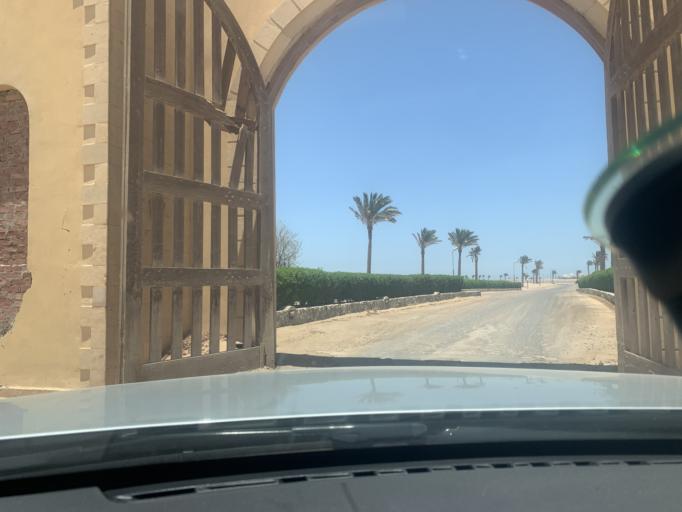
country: EG
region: Red Sea
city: El Gouna
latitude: 27.3960
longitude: 33.6488
